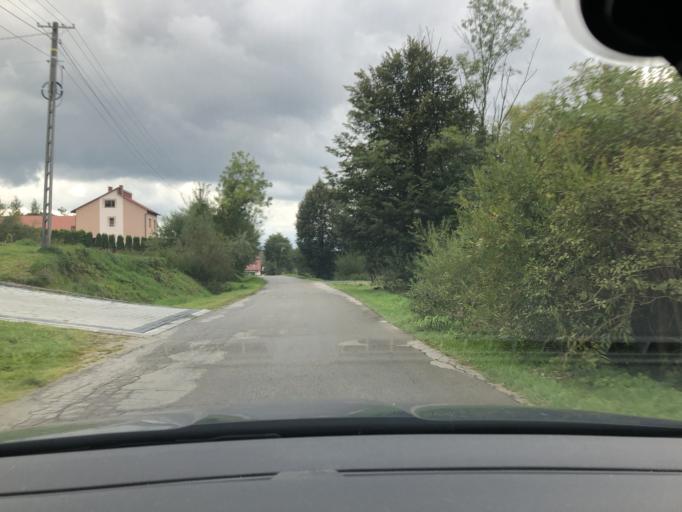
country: PL
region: Silesian Voivodeship
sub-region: Powiat zywiecki
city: Slemien
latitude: 49.7258
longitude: 19.4033
